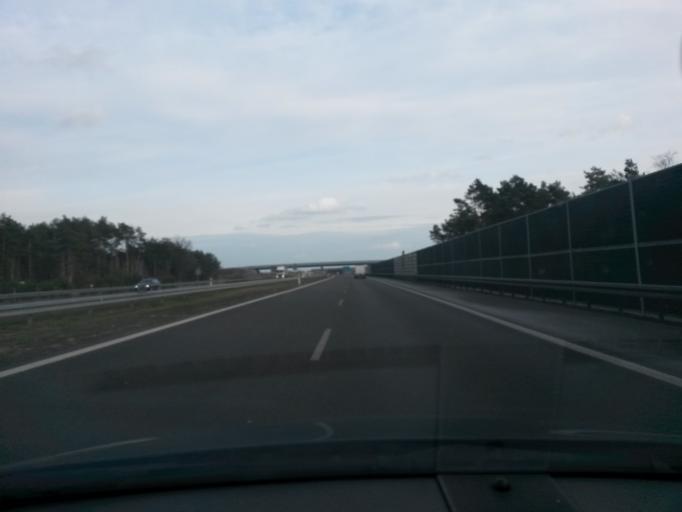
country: PL
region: Greater Poland Voivodeship
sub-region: Powiat kolski
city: Dabie
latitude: 52.0763
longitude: 18.8044
